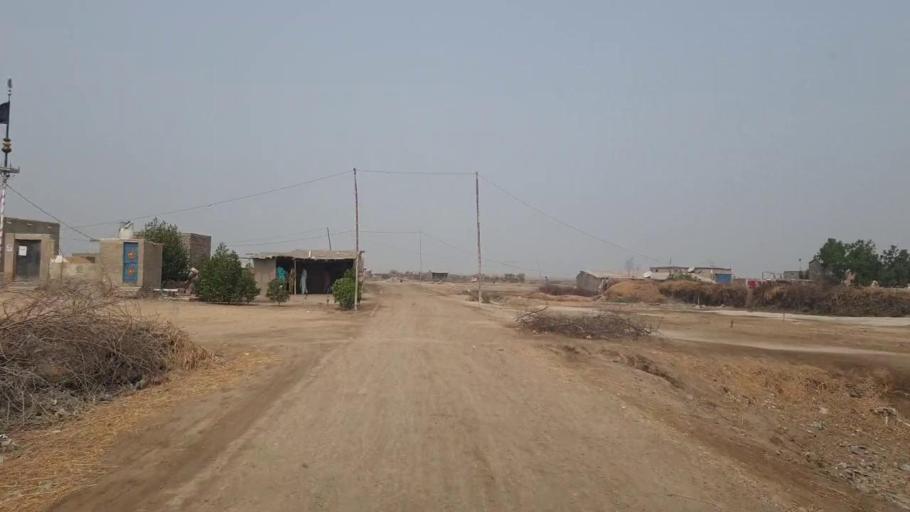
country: PK
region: Sindh
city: Kario
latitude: 24.6600
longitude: 68.6397
